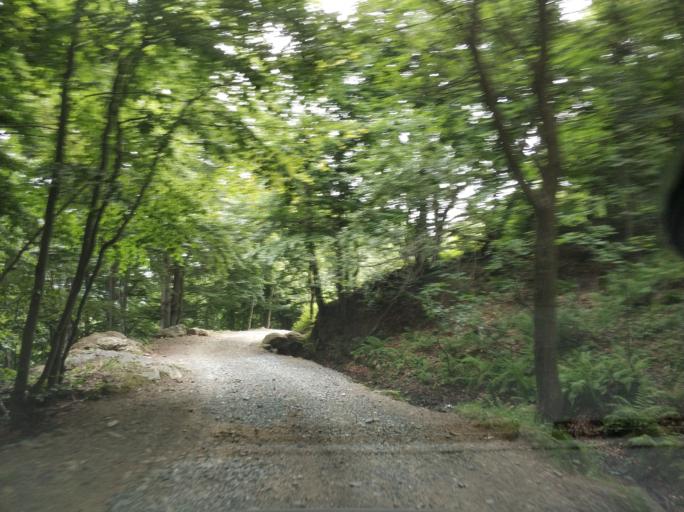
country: IT
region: Piedmont
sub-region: Provincia di Torino
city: Viu
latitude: 45.1979
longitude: 7.3640
